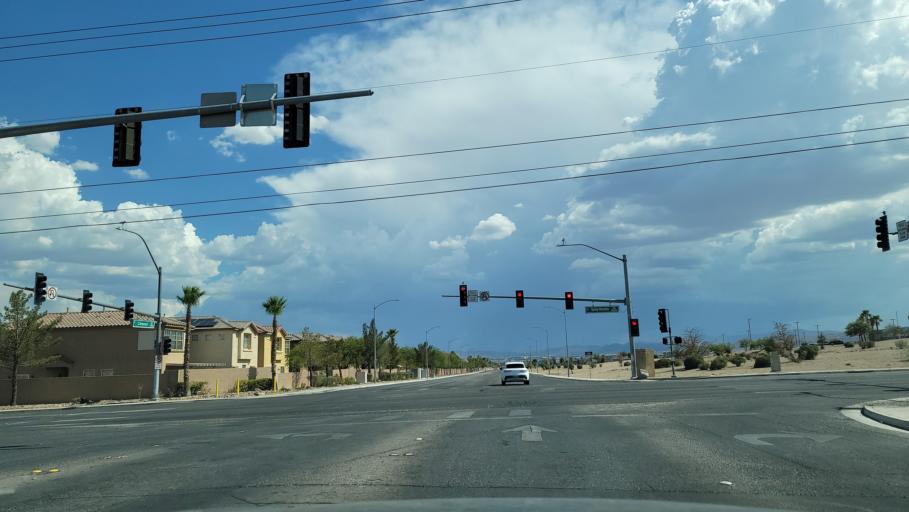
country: US
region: Nevada
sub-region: Clark County
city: Spring Valley
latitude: 36.1260
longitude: -115.2700
